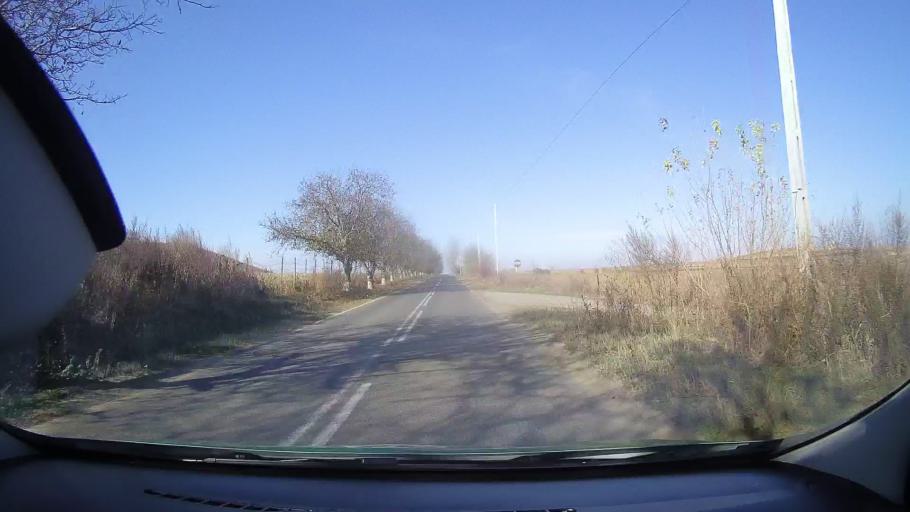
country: RO
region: Tulcea
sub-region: Oras Babadag
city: Babadag
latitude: 44.8808
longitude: 28.7456
